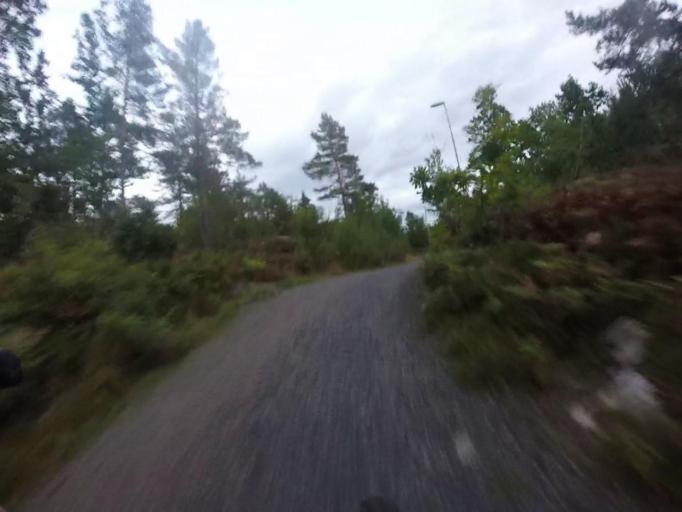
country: SE
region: Vaestra Goetaland
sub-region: Trollhattan
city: Trollhattan
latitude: 58.2898
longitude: 12.2619
